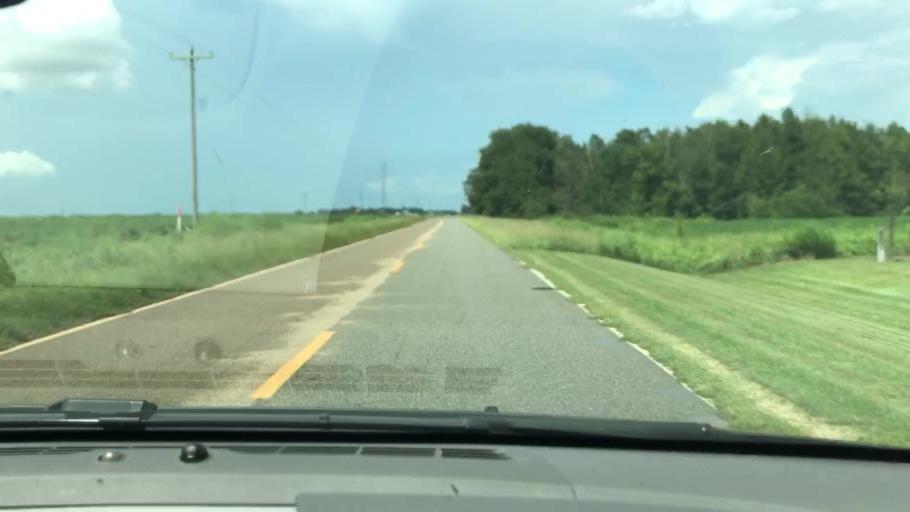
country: US
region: Georgia
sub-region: Seminole County
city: Donalsonville
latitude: 31.0960
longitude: -84.9962
